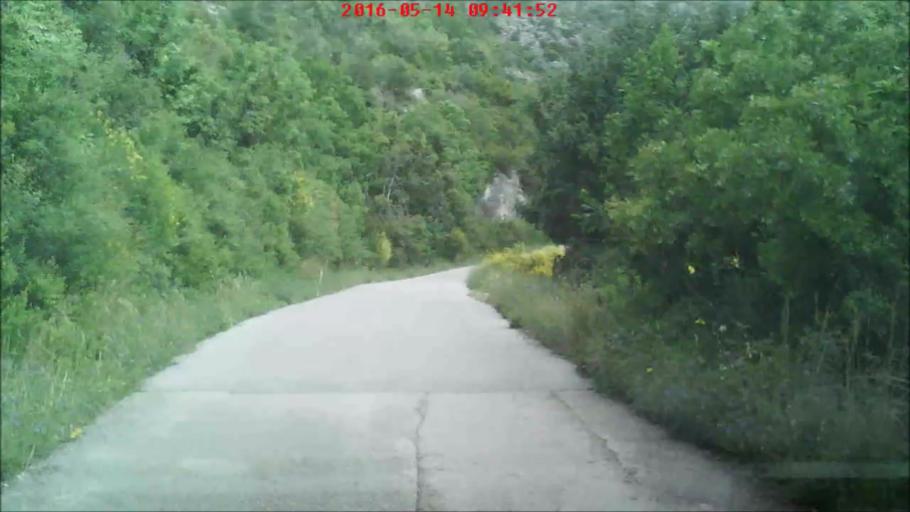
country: HR
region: Dubrovacko-Neretvanska
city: Podgora
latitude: 42.7888
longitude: 17.8986
